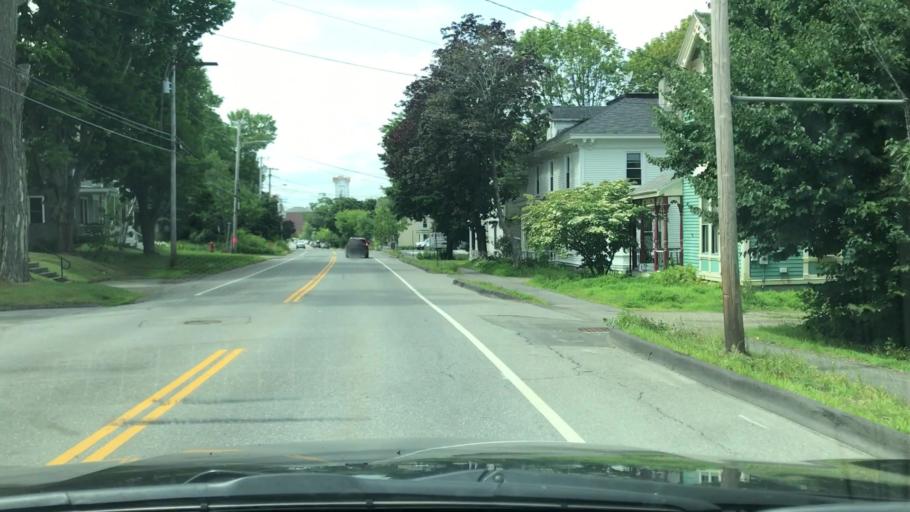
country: US
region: Maine
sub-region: Waldo County
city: Belfast
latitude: 44.4233
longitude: -69.0014
